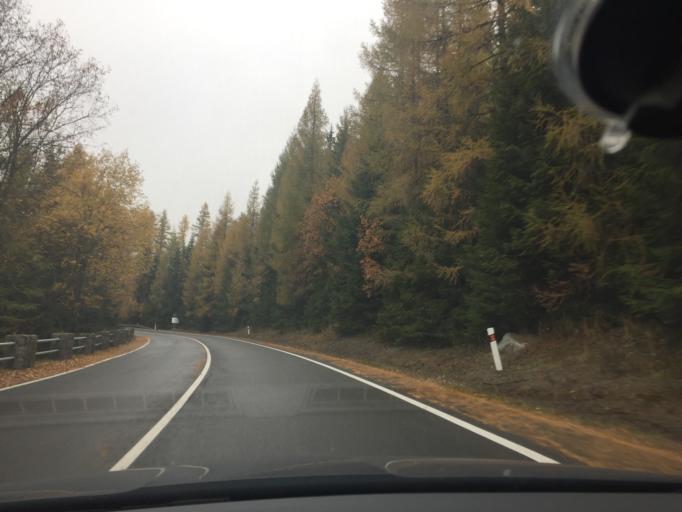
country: SK
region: Presovsky
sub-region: Okres Poprad
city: Strba
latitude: 49.1115
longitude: 20.0748
